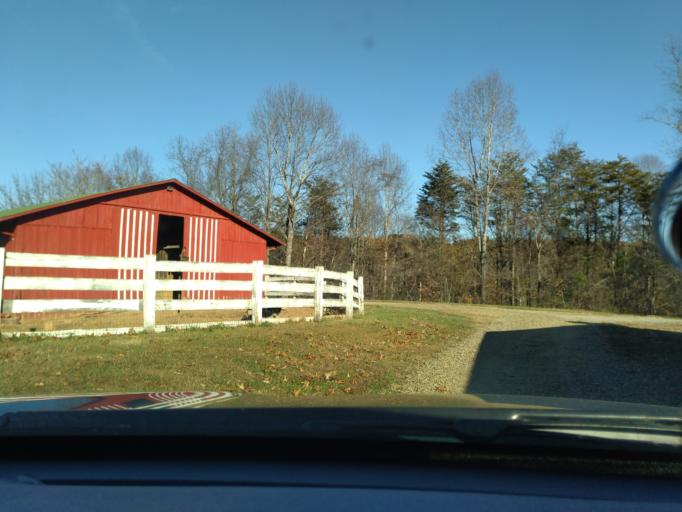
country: US
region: Virginia
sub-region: Floyd County
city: Floyd
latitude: 36.8379
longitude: -80.1821
